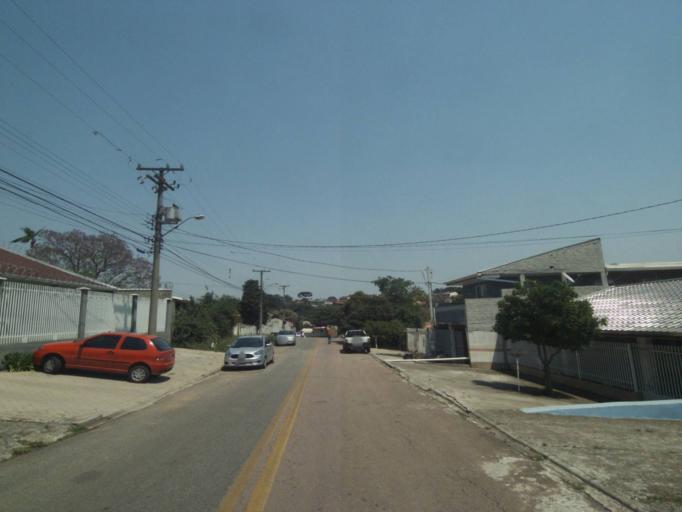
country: BR
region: Parana
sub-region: Sao Jose Dos Pinhais
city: Sao Jose dos Pinhais
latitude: -25.5066
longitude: -49.2675
